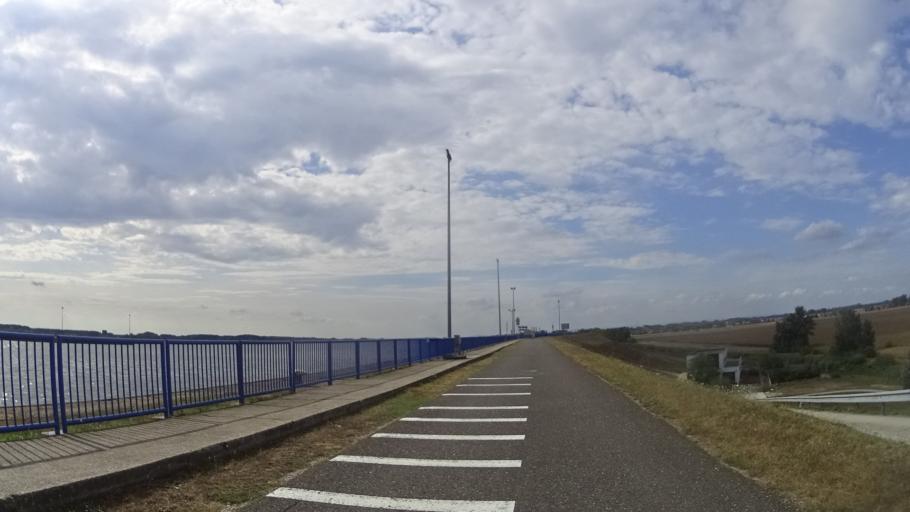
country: SK
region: Trnavsky
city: Gabcikovo
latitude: 47.8882
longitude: 17.5355
